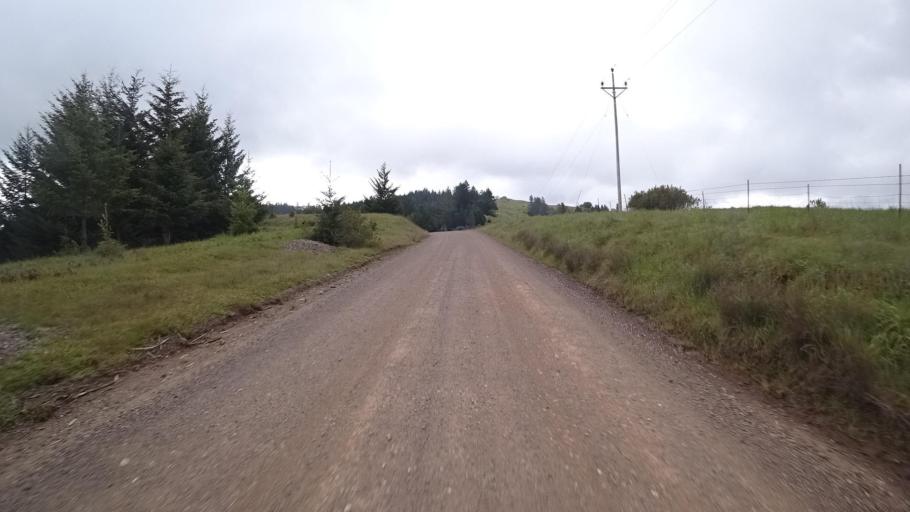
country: US
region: California
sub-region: Humboldt County
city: Redway
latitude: 40.2181
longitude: -123.7544
